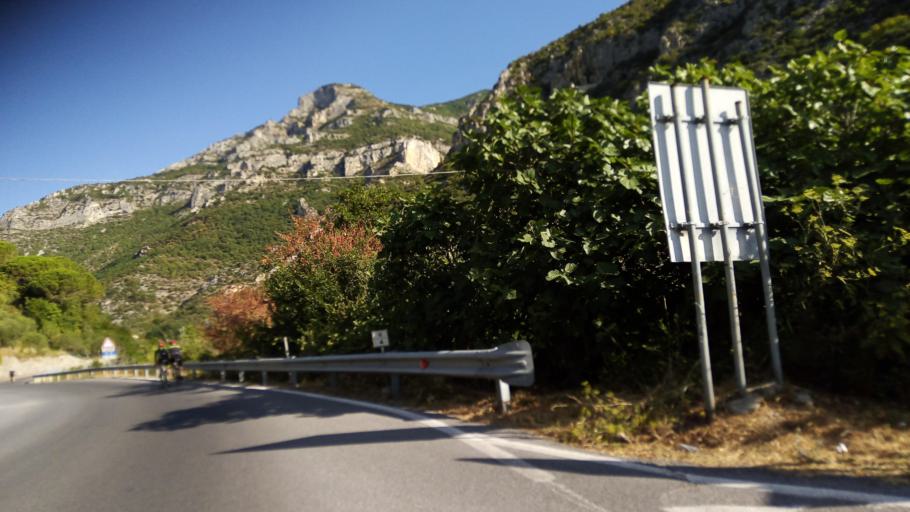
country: IT
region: Liguria
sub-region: Provincia di Savona
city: Toirano
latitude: 44.1309
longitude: 8.2028
